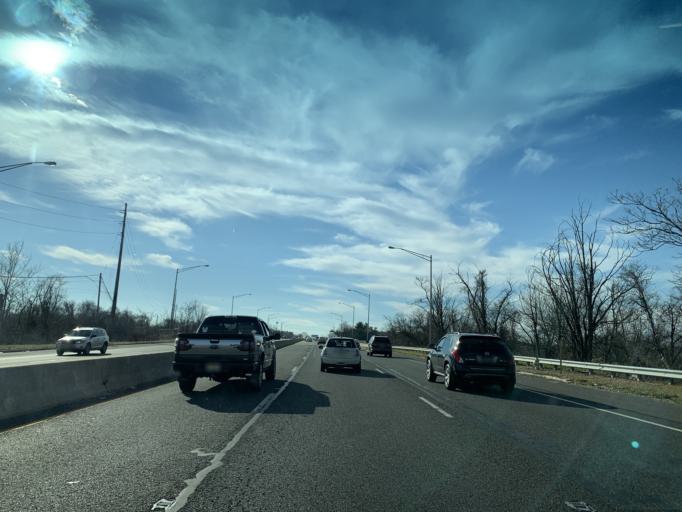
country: US
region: New Jersey
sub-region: Burlington County
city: Delanco
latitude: 40.0301
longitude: -74.9306
